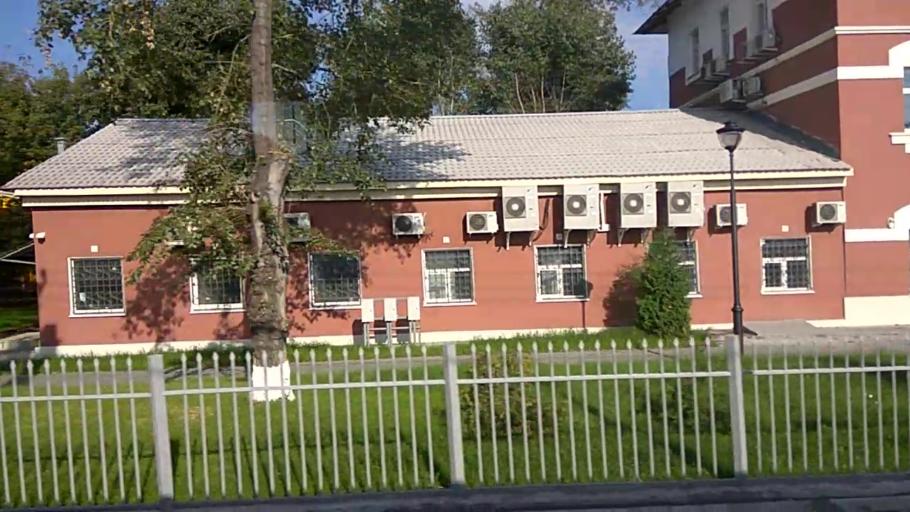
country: RU
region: Moskovskaya
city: Kozhukhovo
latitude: 55.7154
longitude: 37.6865
